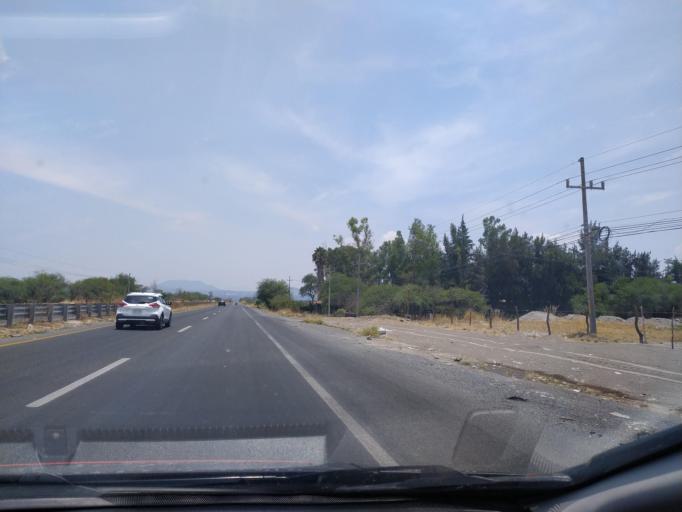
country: MX
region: Jalisco
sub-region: Acatlan de Juarez
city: Villa de los Ninos
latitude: 20.3695
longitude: -103.5923
